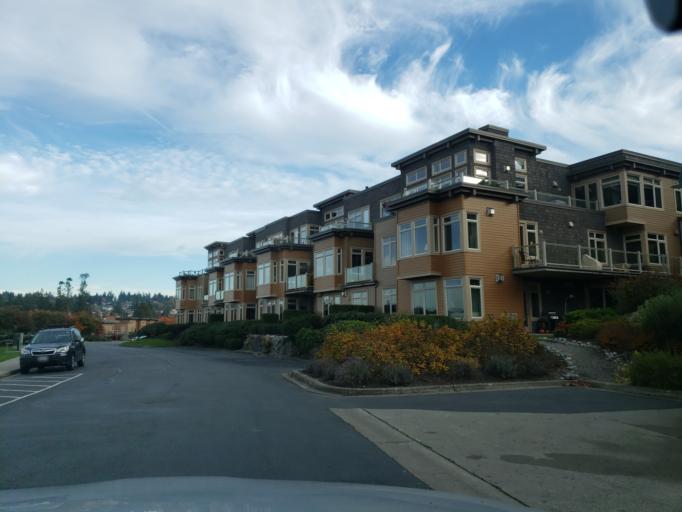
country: US
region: Washington
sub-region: Snohomish County
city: Woodway
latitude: 47.8044
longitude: -122.3895
